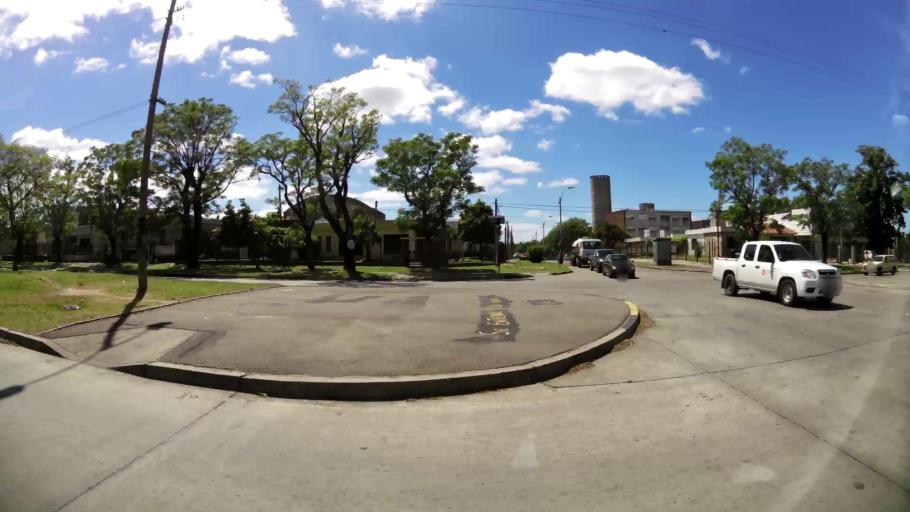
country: UY
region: Montevideo
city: Montevideo
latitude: -34.8553
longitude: -56.1498
